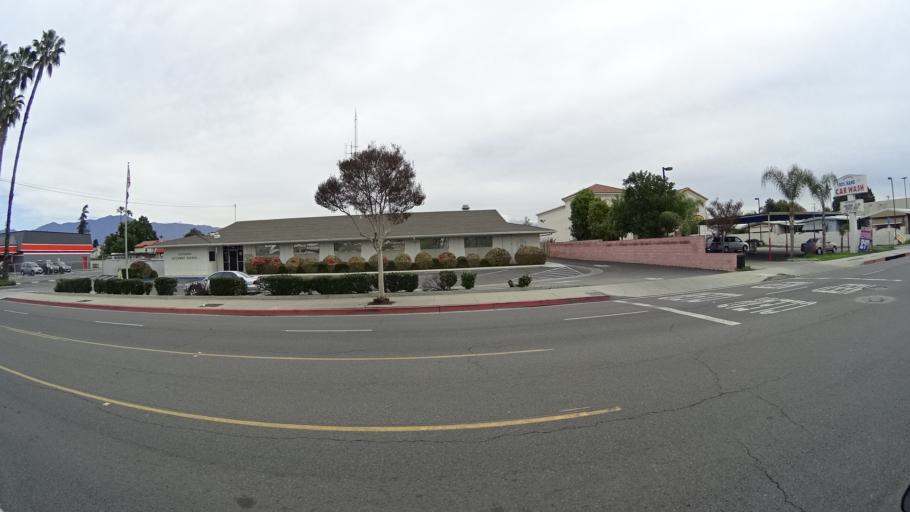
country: US
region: California
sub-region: Los Angeles County
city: West Puente Valley
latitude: 34.0655
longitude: -117.9700
